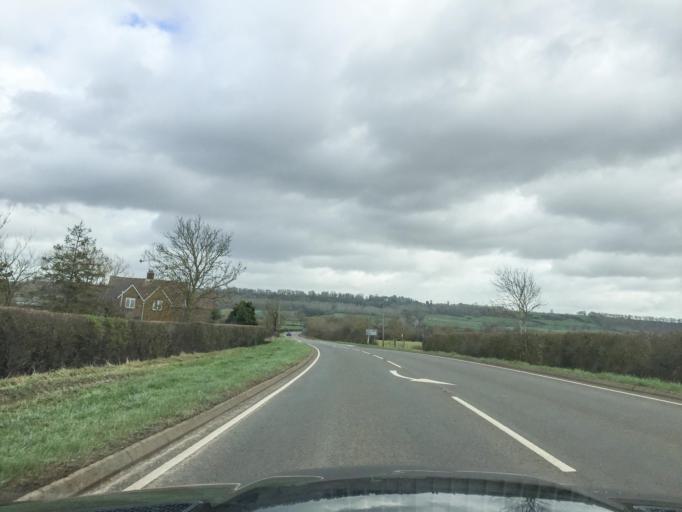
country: GB
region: England
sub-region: Warwickshire
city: Wellesbourne Mountford
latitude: 52.1199
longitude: -1.5033
